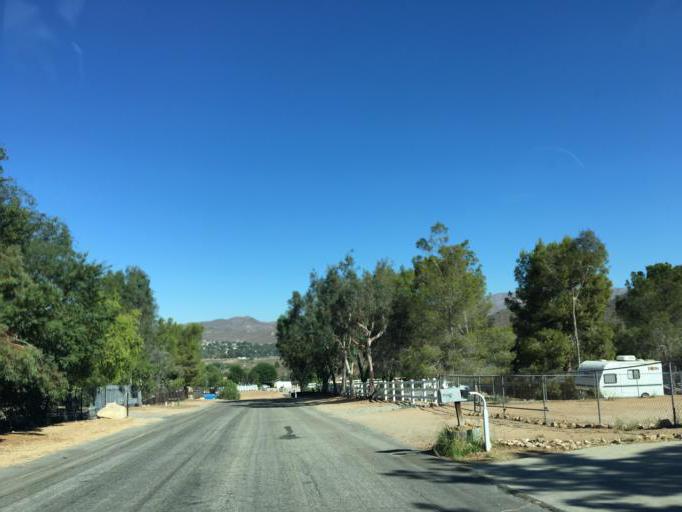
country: US
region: California
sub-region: Los Angeles County
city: Acton
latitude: 34.4552
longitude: -118.1821
